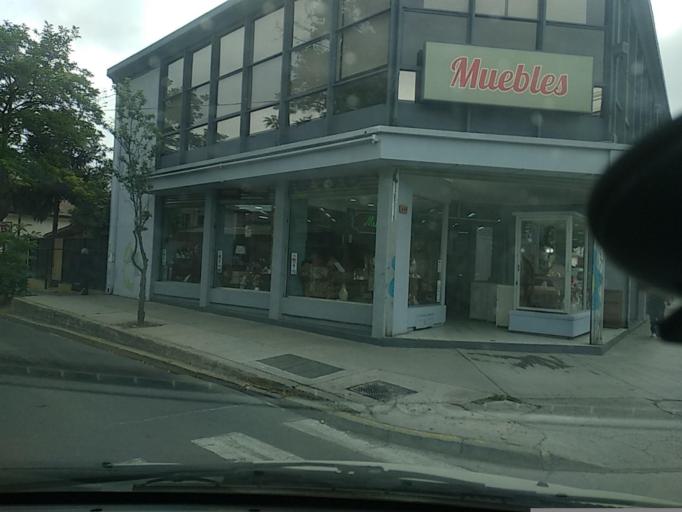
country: CL
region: Valparaiso
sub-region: Provincia de Marga Marga
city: Villa Alemana
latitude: -33.0437
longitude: -71.3766
